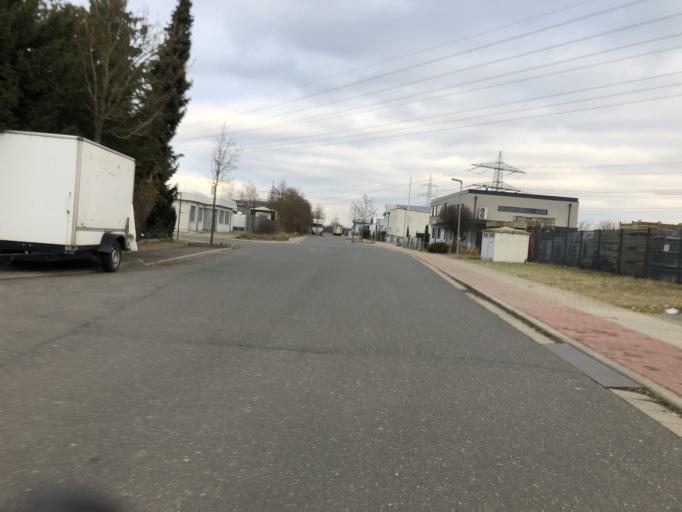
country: DE
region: Baden-Wuerttemberg
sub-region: Karlsruhe Region
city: Neulussheim
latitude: 49.2903
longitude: 8.5100
